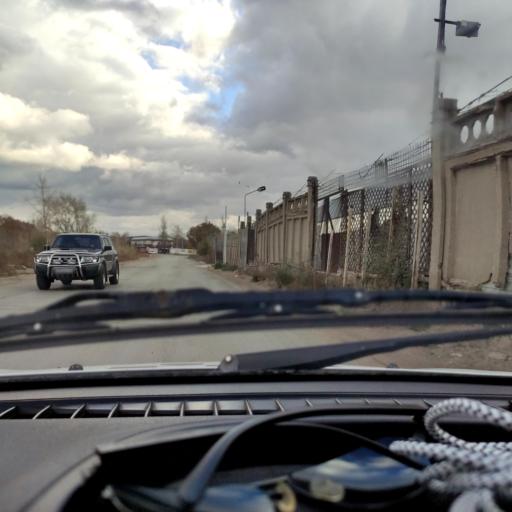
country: RU
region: Samara
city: Zhigulevsk
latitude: 53.4770
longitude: 49.4974
